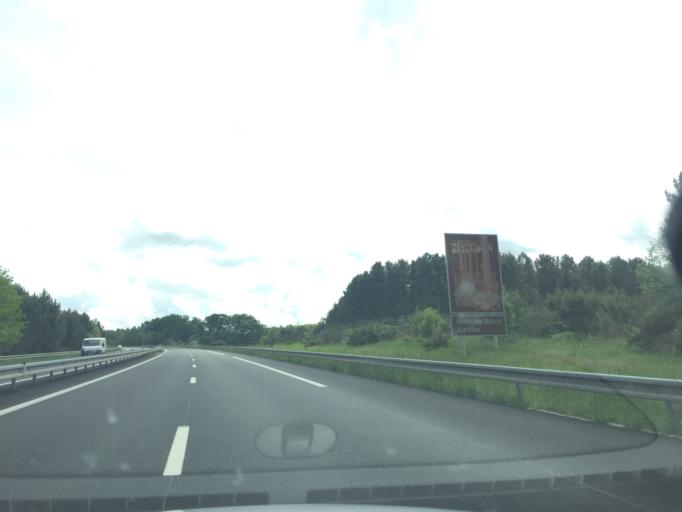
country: FR
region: Pays de la Loire
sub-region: Departement de la Sarthe
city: Ecommoy
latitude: 47.8575
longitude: 0.2974
